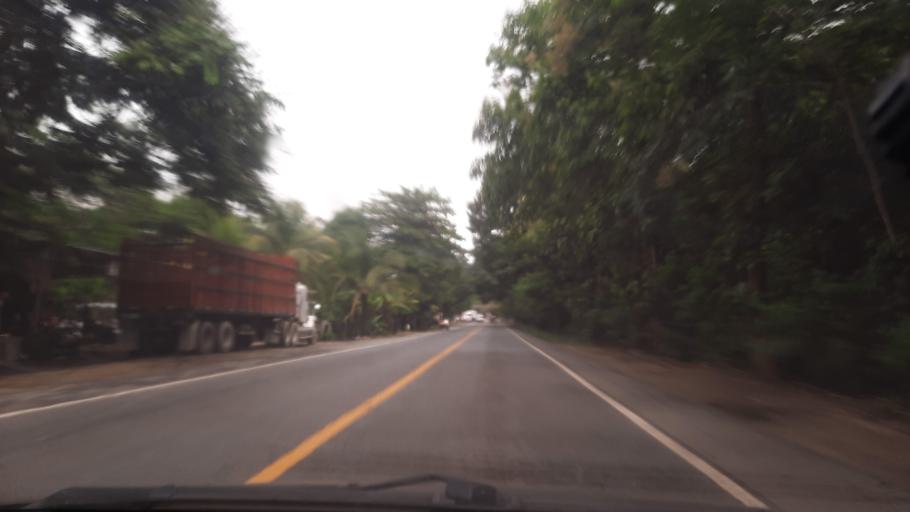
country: GT
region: Izabal
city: Morales
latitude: 15.4641
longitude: -88.9120
